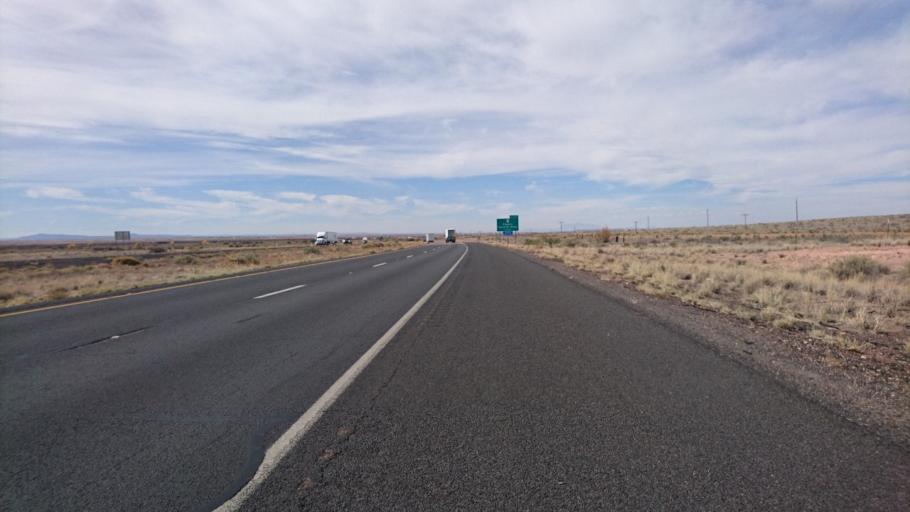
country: US
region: Arizona
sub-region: Navajo County
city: Winslow
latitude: 35.0066
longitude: -110.6181
